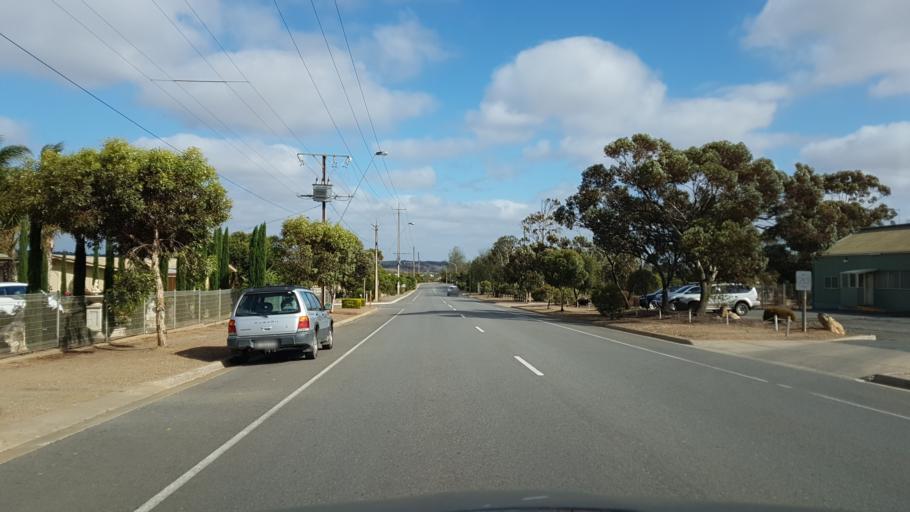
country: AU
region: South Australia
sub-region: Murray Bridge
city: Murray Bridge
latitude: -35.1191
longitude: 139.2495
